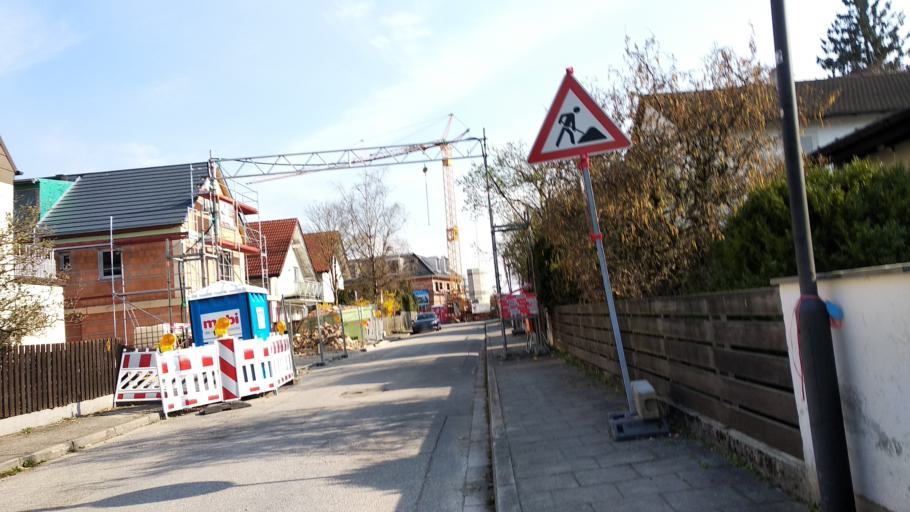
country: DE
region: Bavaria
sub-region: Upper Bavaria
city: Haar
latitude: 48.1020
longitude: 11.7278
